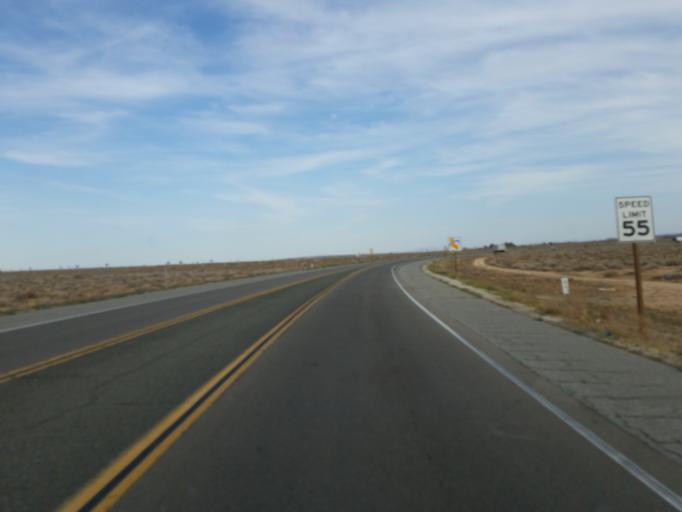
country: US
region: California
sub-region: Kern County
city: Boron
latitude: 35.0095
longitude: -117.6238
